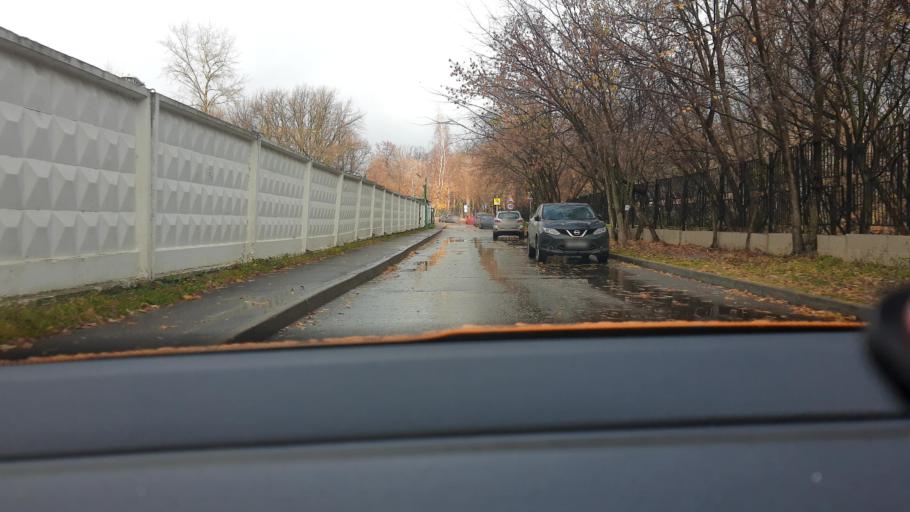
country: RU
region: Moskovskaya
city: Bol'shaya Setun'
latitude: 55.7434
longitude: 37.4325
